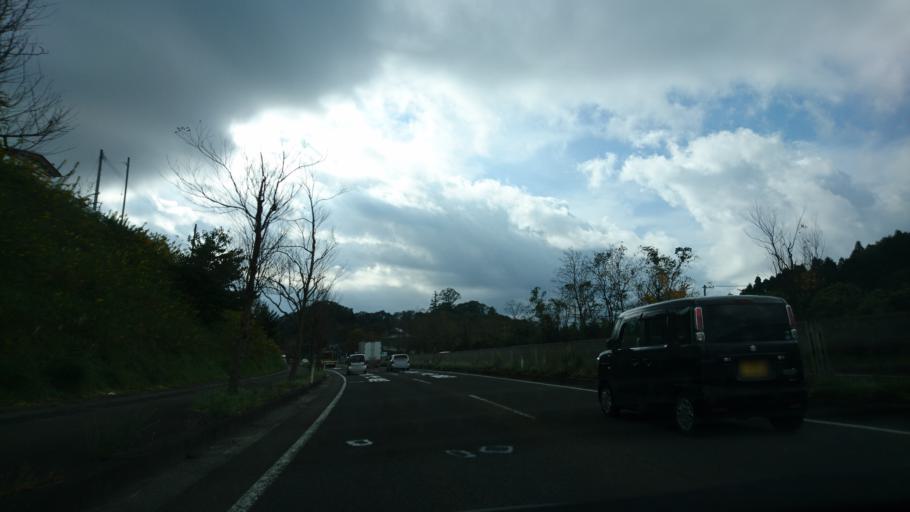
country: JP
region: Miyagi
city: Tomiya
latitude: 38.3795
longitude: 140.8726
